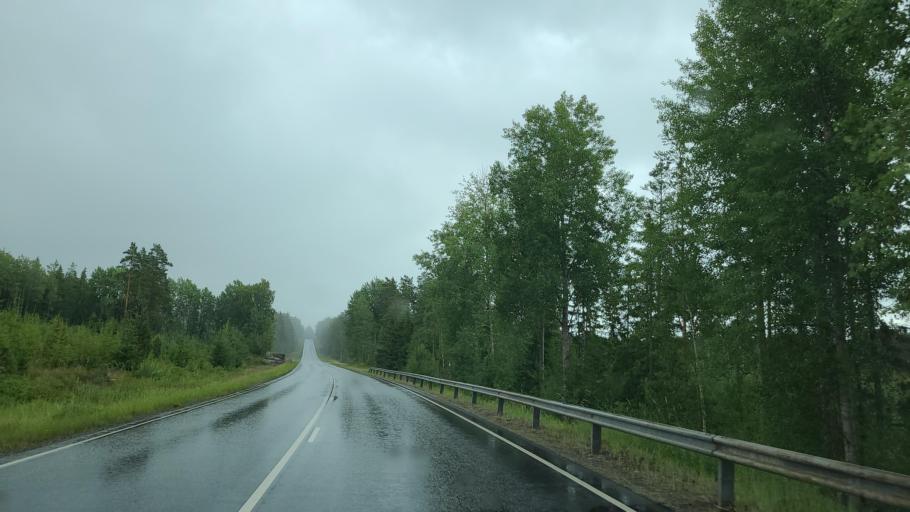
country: FI
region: Varsinais-Suomi
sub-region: Aboland-Turunmaa
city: Kimito
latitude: 60.2042
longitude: 22.6493
